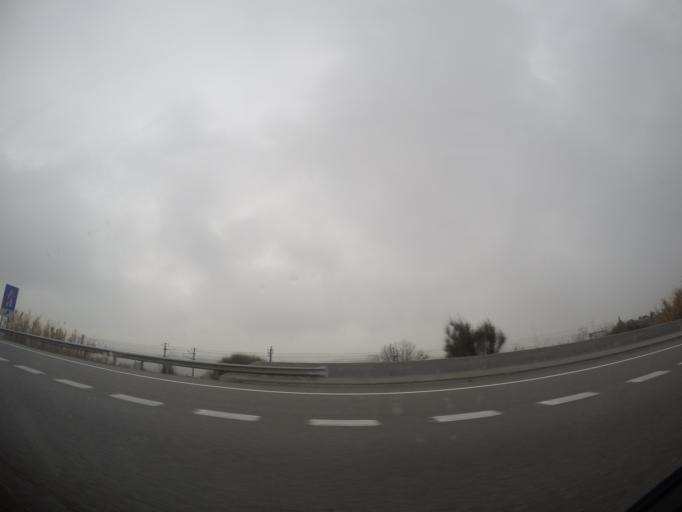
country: ES
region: Catalonia
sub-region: Provincia de Barcelona
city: Sant Sadurni d'Anoia
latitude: 41.4189
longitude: 1.7957
